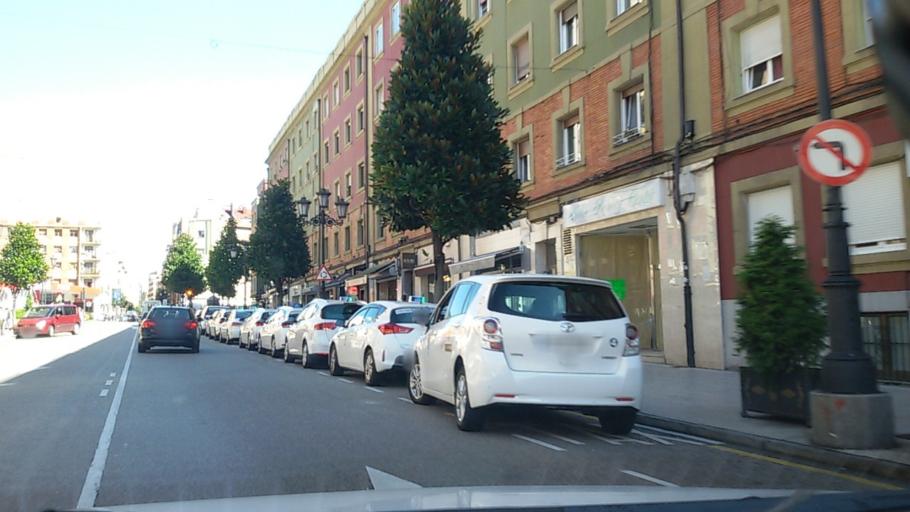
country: ES
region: Asturias
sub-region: Province of Asturias
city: Oviedo
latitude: 43.3697
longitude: -5.8382
